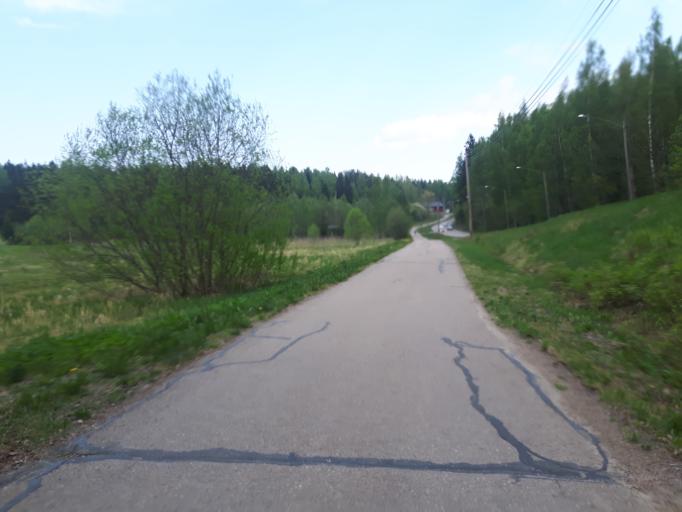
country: FI
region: Uusimaa
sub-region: Porvoo
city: Porvoo
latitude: 60.4003
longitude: 25.7269
